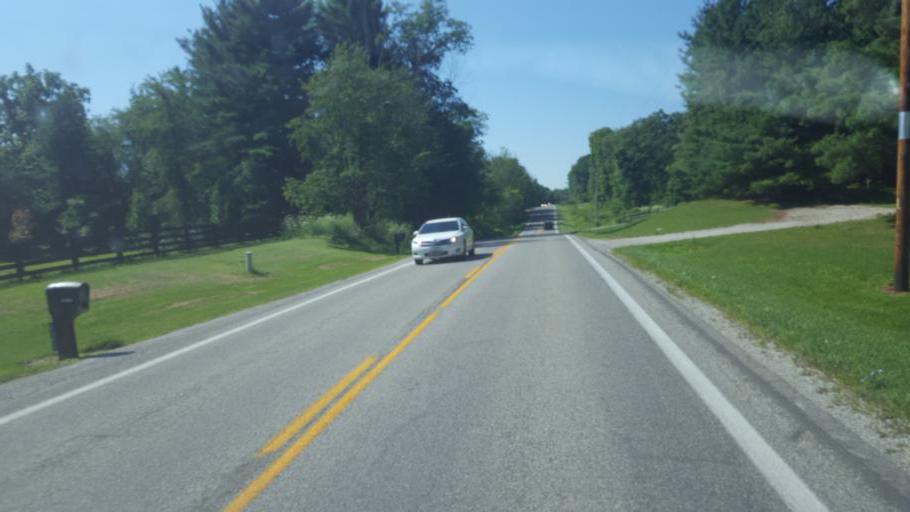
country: US
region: Ohio
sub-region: Morrow County
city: Mount Gilead
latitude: 40.5081
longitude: -82.8176
